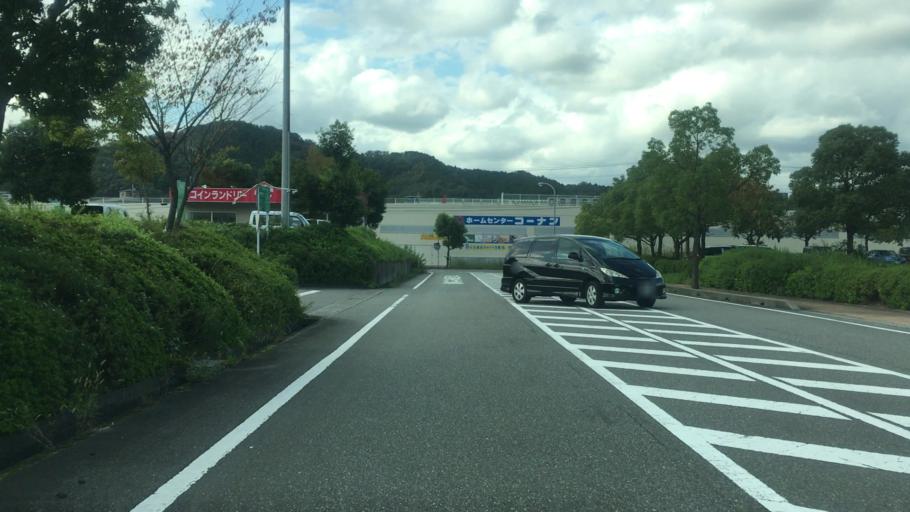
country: JP
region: Hyogo
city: Toyooka
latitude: 35.3309
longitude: 134.8634
